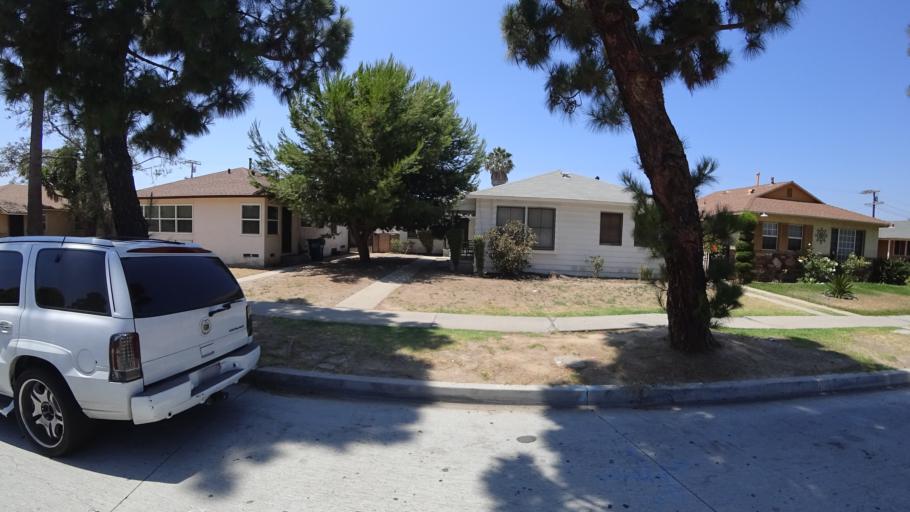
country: US
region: California
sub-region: Los Angeles County
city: West Athens
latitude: 33.9280
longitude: -118.3265
